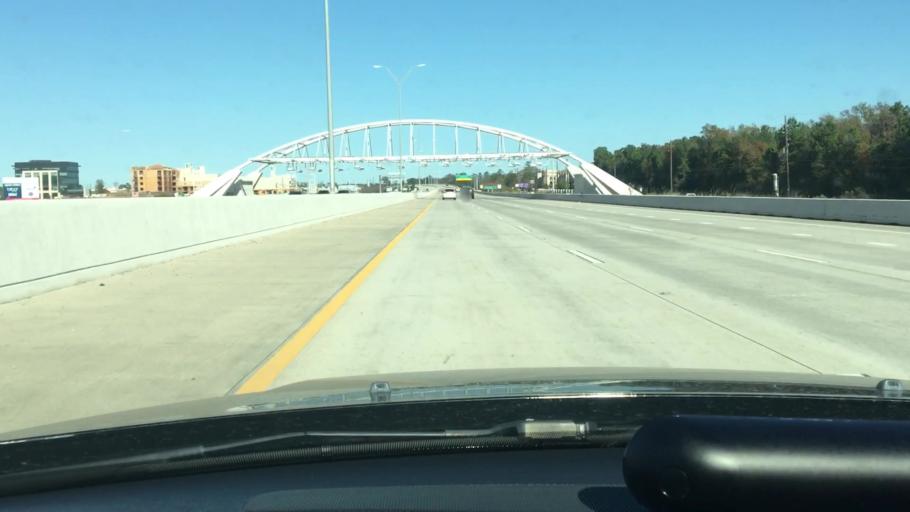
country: US
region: Texas
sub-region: Harris County
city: Sheldon
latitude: 29.9144
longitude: -95.2011
